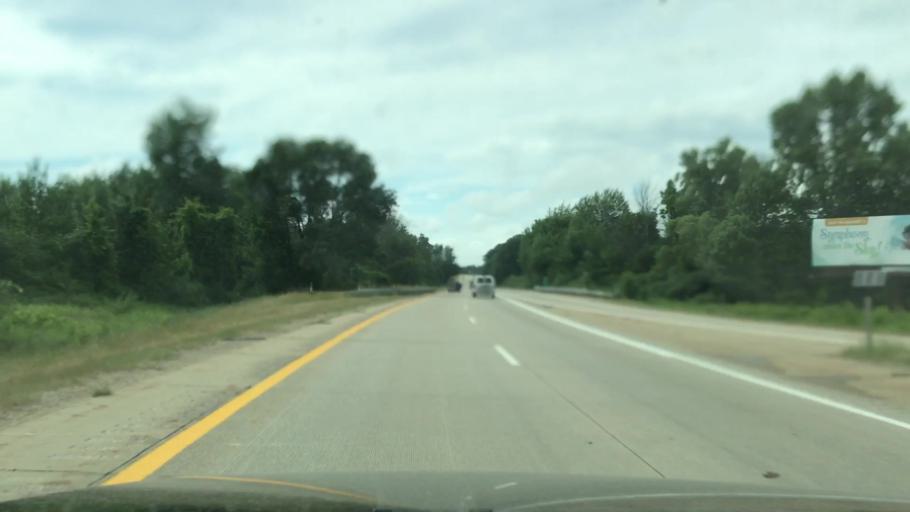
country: US
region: Michigan
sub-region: Kent County
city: Walker
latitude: 43.0196
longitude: -85.7683
